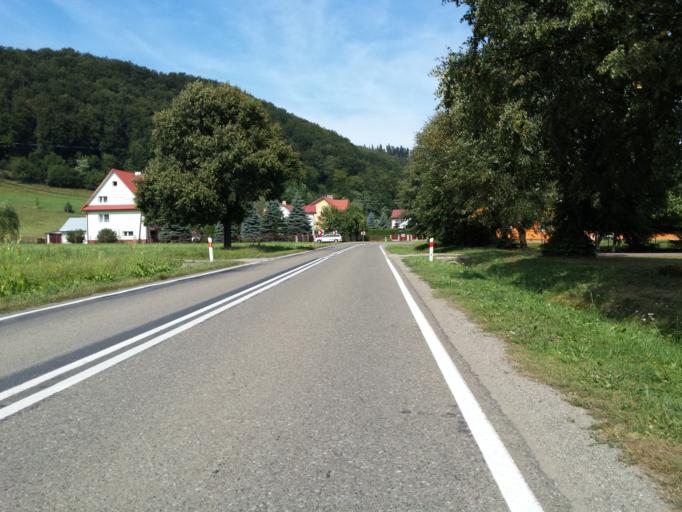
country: PL
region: Subcarpathian Voivodeship
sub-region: Powiat leski
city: Baligrod
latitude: 49.3933
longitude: 22.2818
